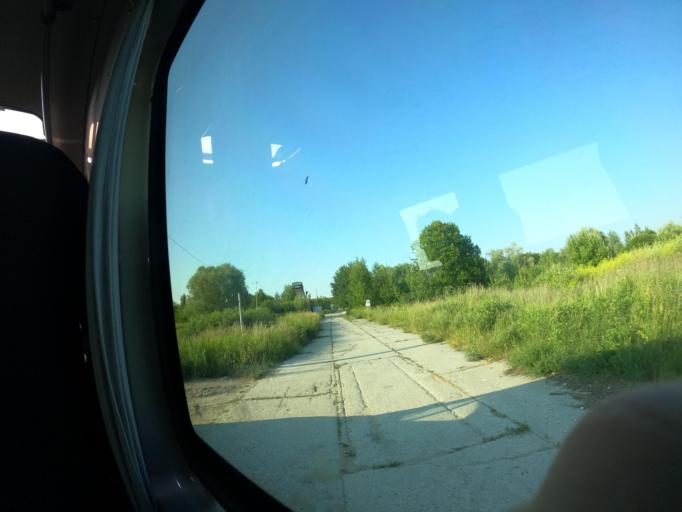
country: RU
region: Moskovskaya
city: Obolensk
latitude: 54.9335
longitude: 37.2497
